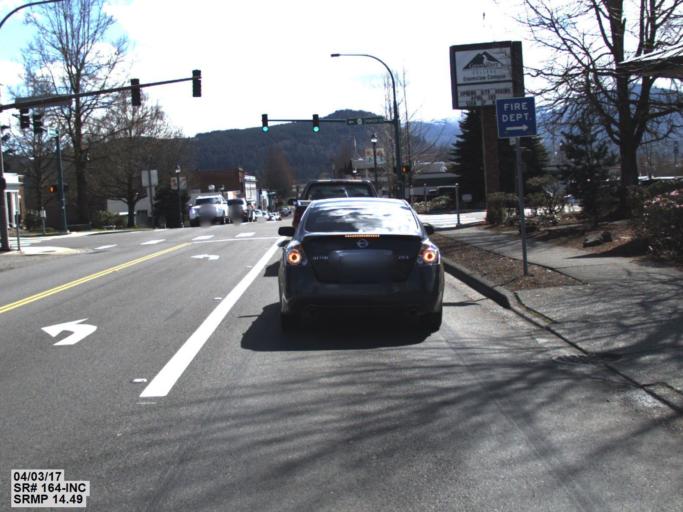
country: US
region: Washington
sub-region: King County
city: Enumclaw
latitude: 47.2047
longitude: -121.9920
